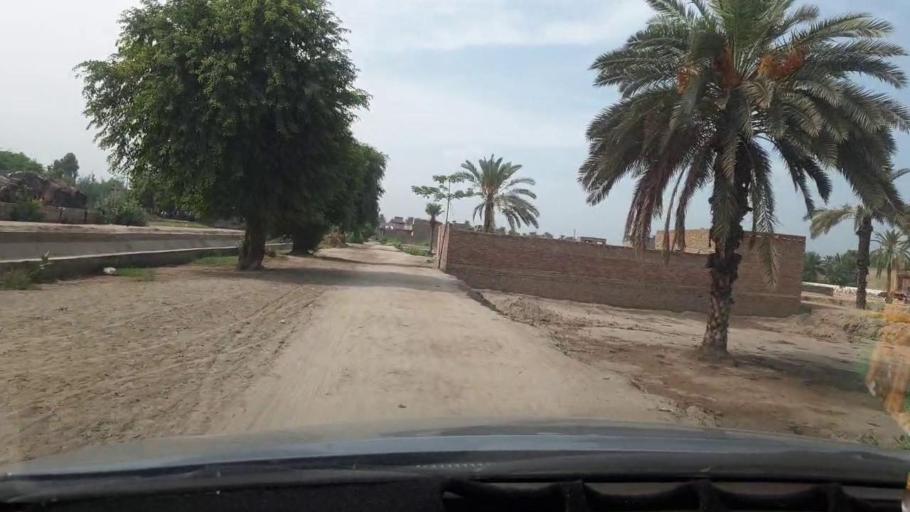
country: PK
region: Sindh
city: Khairpur
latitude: 27.5103
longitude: 68.7599
